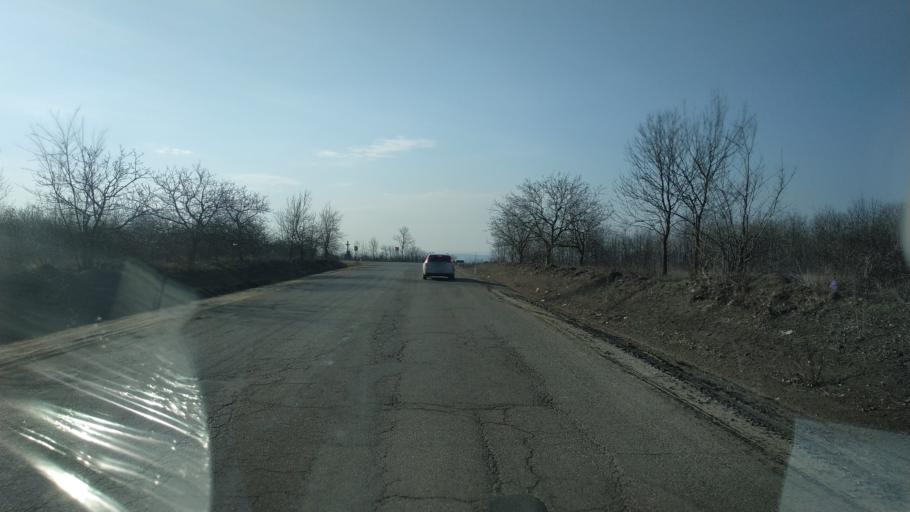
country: MD
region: Chisinau
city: Singera
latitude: 46.8592
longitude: 29.0315
